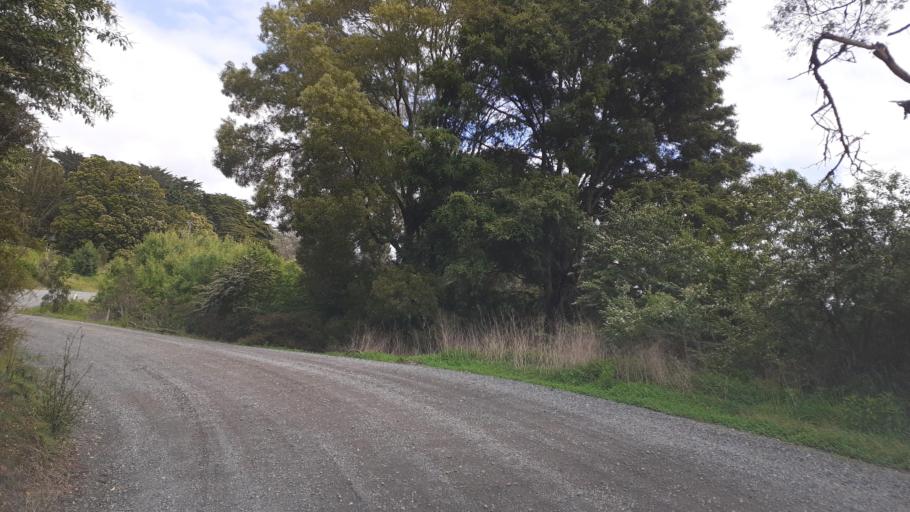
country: NZ
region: Northland
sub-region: Far North District
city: Kawakawa
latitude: -35.5157
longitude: 174.0823
